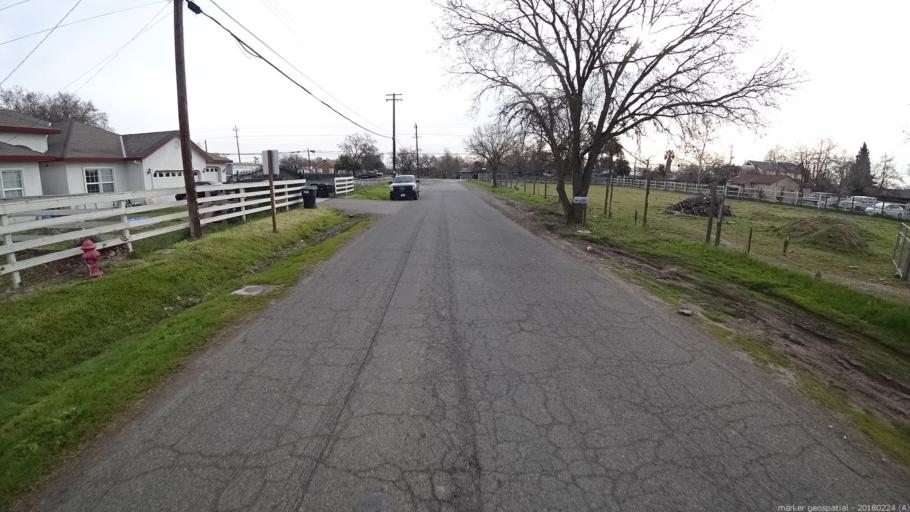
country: US
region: California
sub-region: Sacramento County
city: Rio Linda
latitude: 38.6767
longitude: -121.4580
